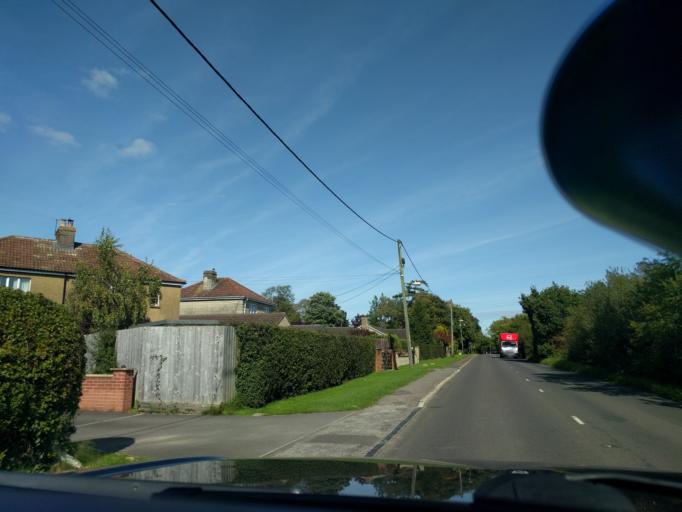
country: GB
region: England
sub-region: Wiltshire
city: Atworth
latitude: 51.3962
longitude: -2.1619
